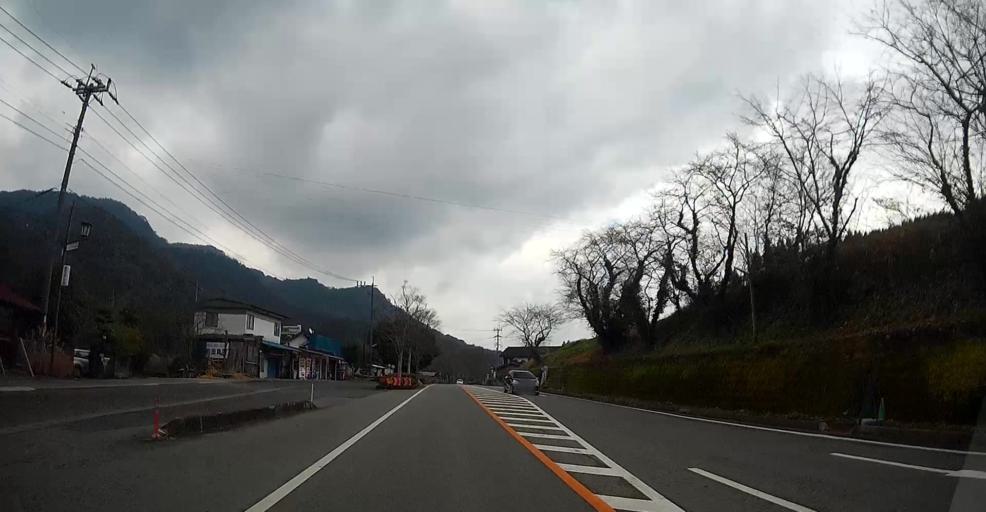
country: JP
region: Kumamoto
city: Matsubase
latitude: 32.6223
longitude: 130.8255
